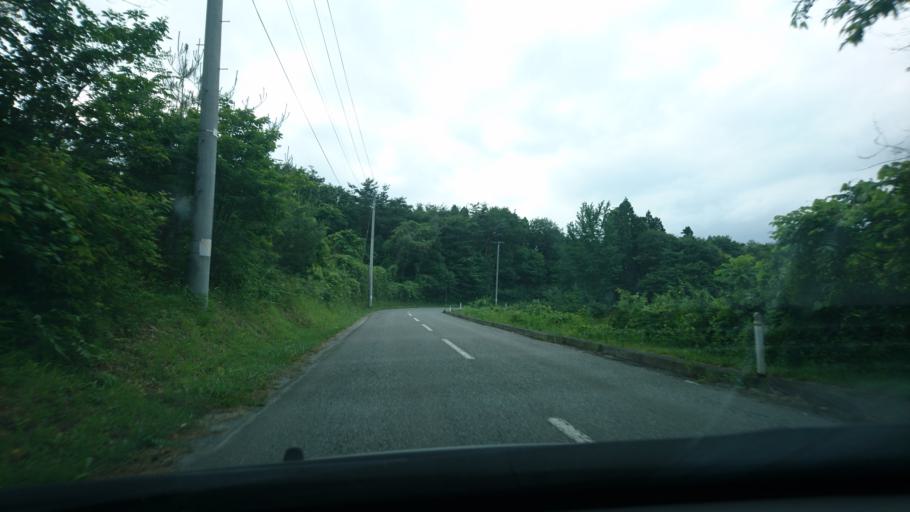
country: JP
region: Iwate
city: Ichinoseki
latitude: 38.9039
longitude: 141.1546
